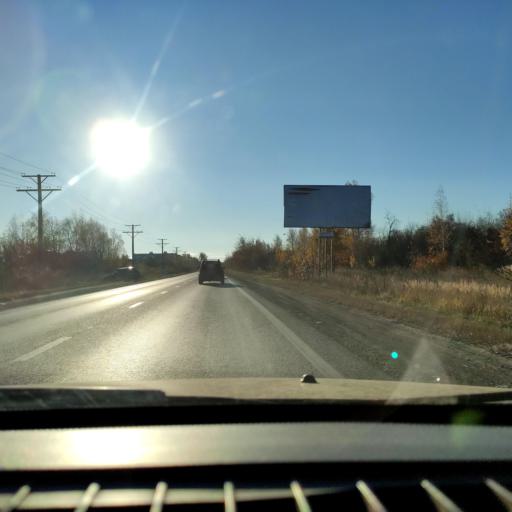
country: RU
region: Samara
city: Tol'yatti
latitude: 53.5562
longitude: 49.3644
